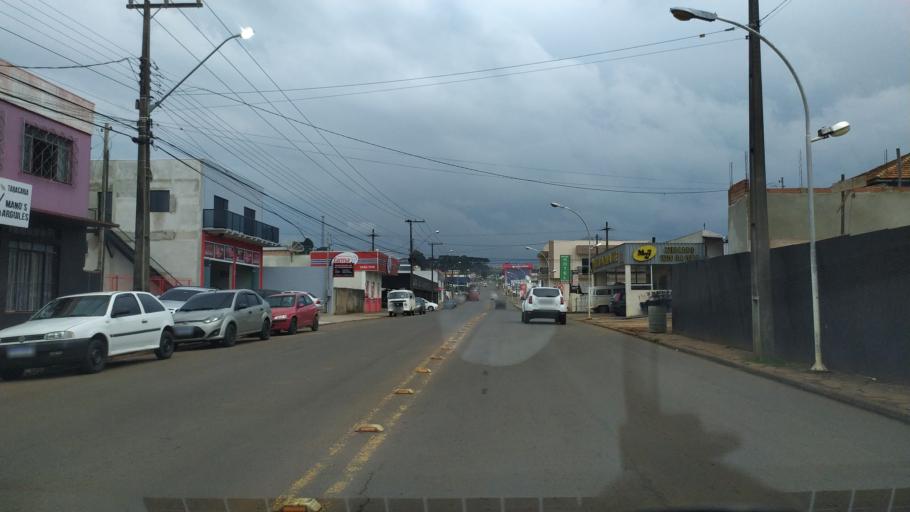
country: BR
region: Parana
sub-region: Palmas
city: Palmas
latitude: -26.4865
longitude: -51.9976
